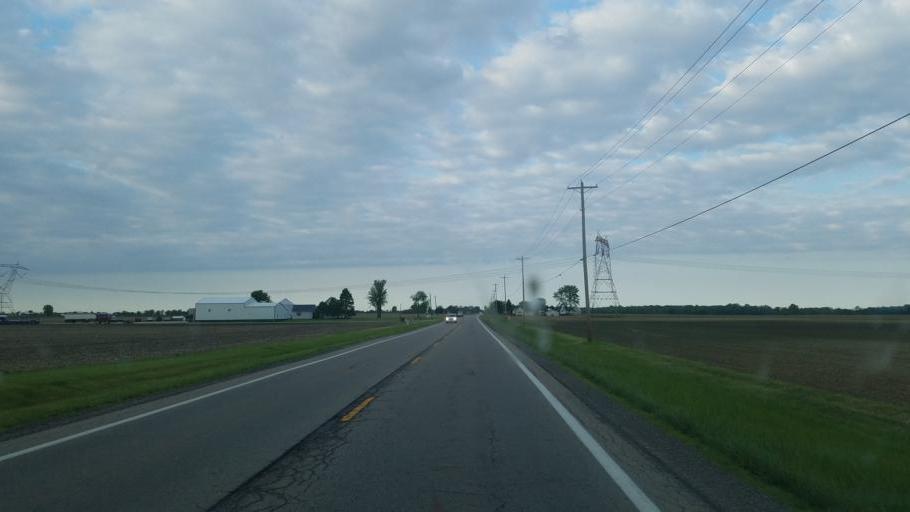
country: US
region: Ohio
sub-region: Madison County
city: Mount Sterling
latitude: 39.7713
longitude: -83.2160
